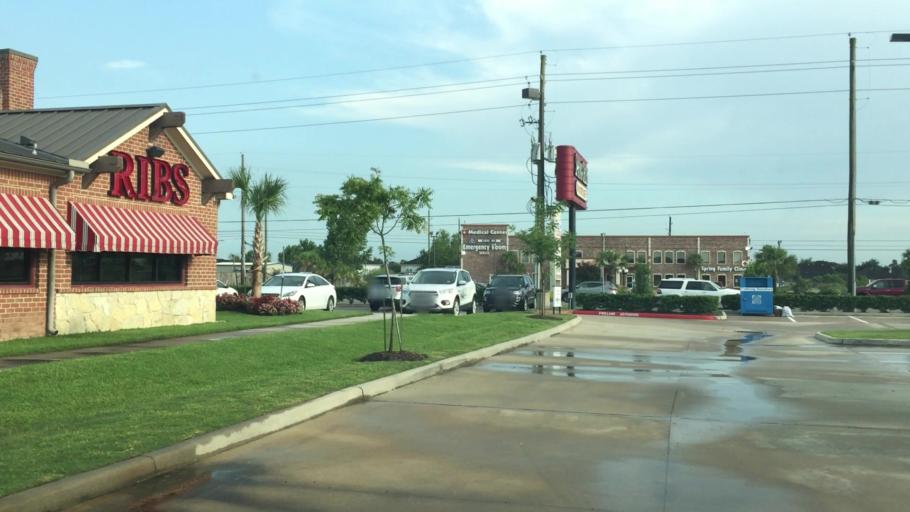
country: US
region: Texas
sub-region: Montgomery County
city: The Woodlands
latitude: 30.0747
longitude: -95.5195
